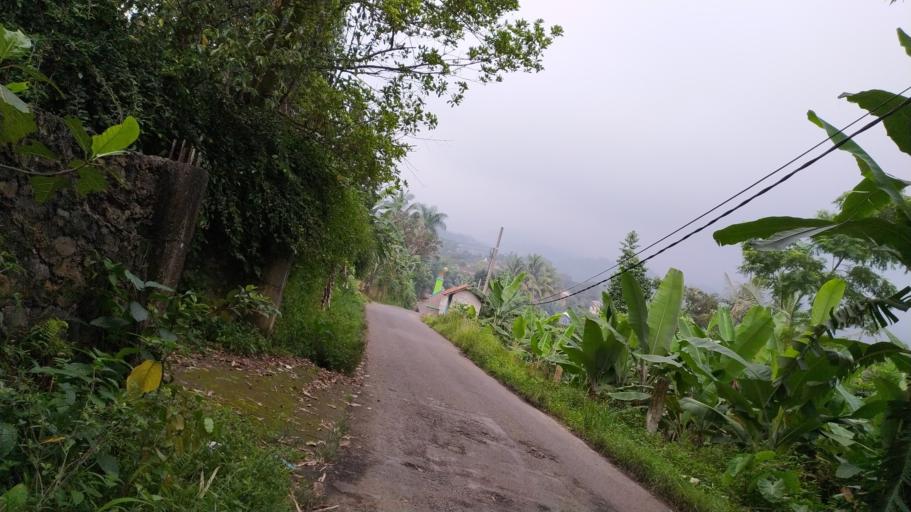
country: ID
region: West Java
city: Ciampea
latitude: -6.6497
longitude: 106.7050
